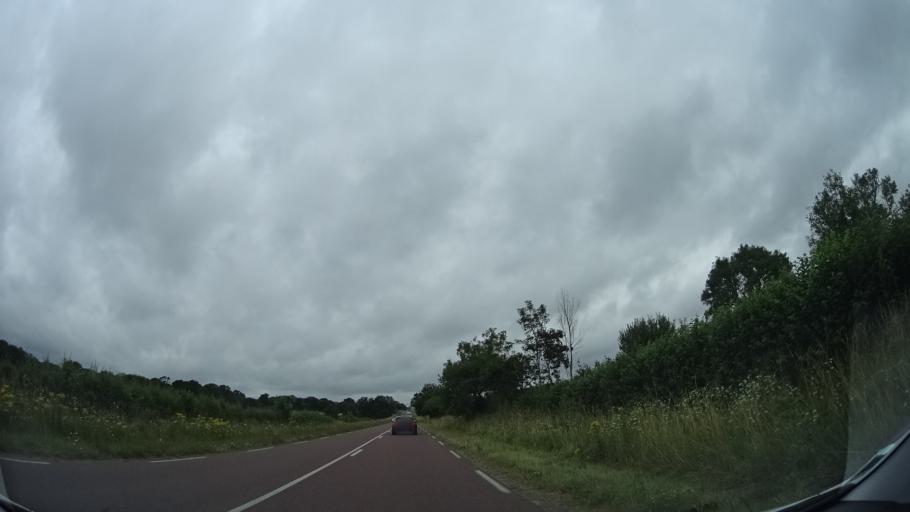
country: FR
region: Lower Normandy
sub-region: Departement de la Manche
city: La Haye-du-Puits
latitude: 49.2735
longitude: -1.5401
